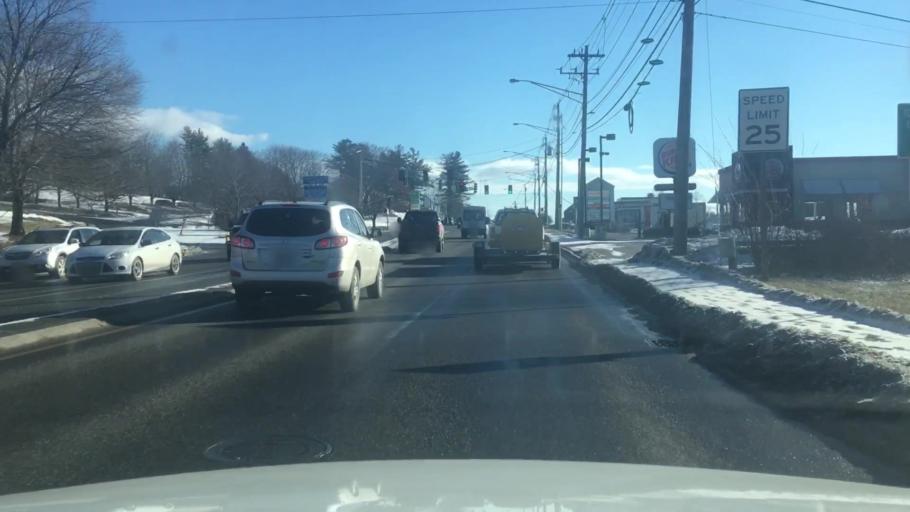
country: US
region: Maine
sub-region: Kennebec County
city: Augusta
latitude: 44.3133
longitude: -69.7961
